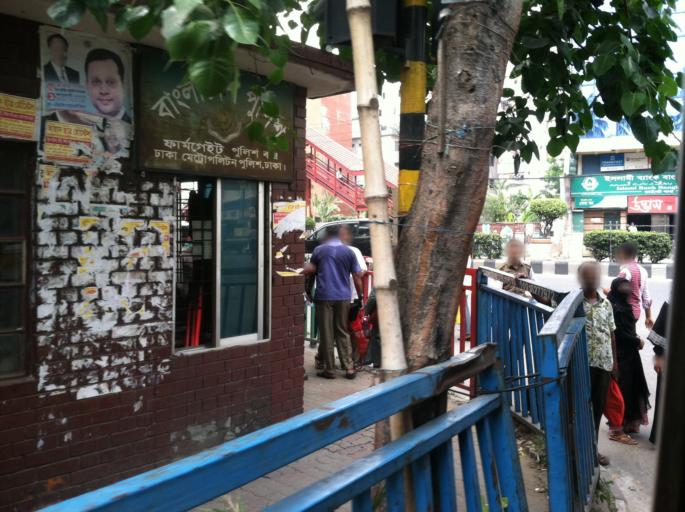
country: BD
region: Dhaka
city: Azimpur
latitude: 23.7593
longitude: 90.3894
